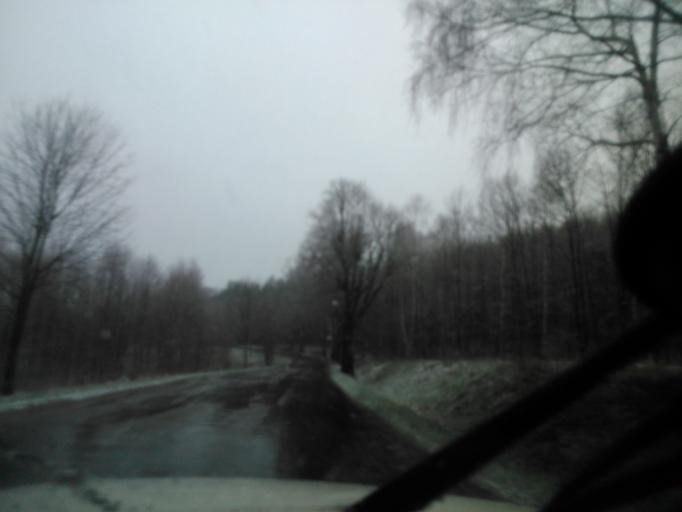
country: PL
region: Warmian-Masurian Voivodeship
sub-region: Powiat ostrodzki
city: Dabrowno
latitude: 53.3888
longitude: 20.0145
